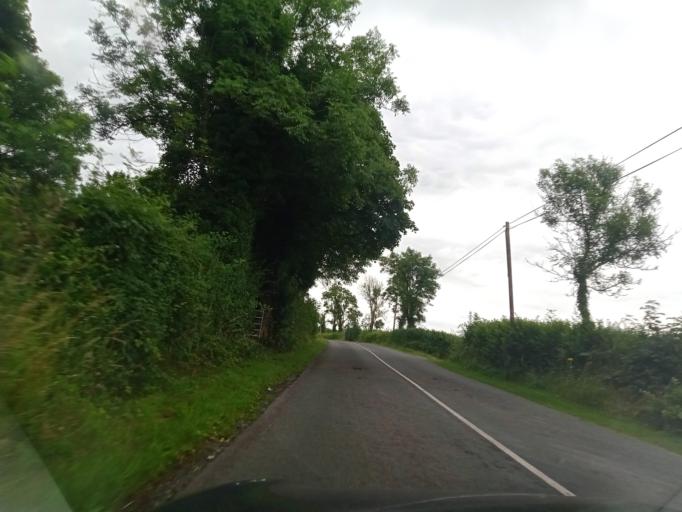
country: IE
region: Leinster
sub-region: Laois
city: Stradbally
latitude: 52.9398
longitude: -7.1985
